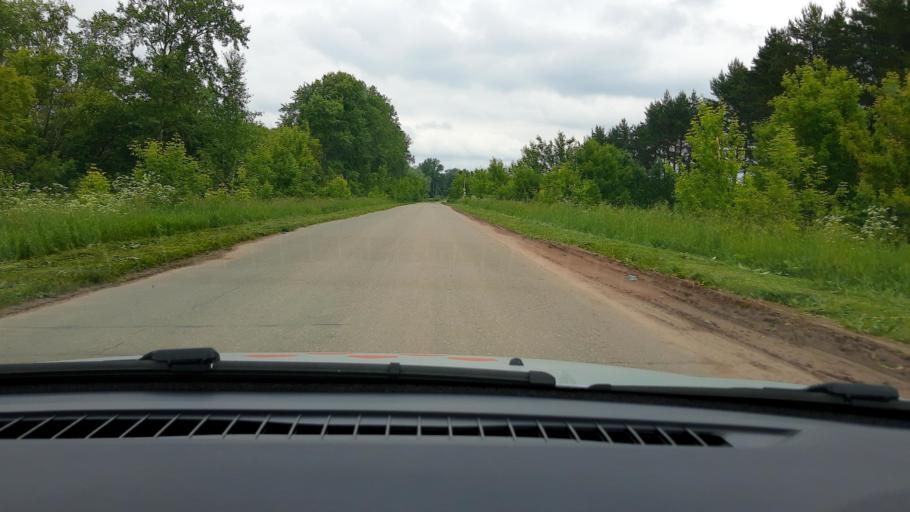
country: RU
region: Nizjnij Novgorod
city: Bogorodsk
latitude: 56.0684
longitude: 43.5036
